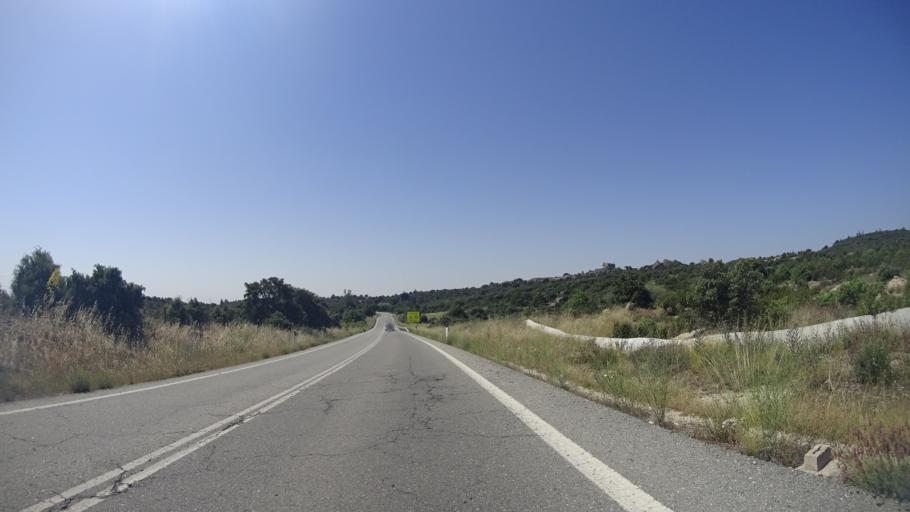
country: ES
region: Madrid
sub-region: Provincia de Madrid
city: Torrelodones
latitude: 40.5975
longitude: -3.9191
